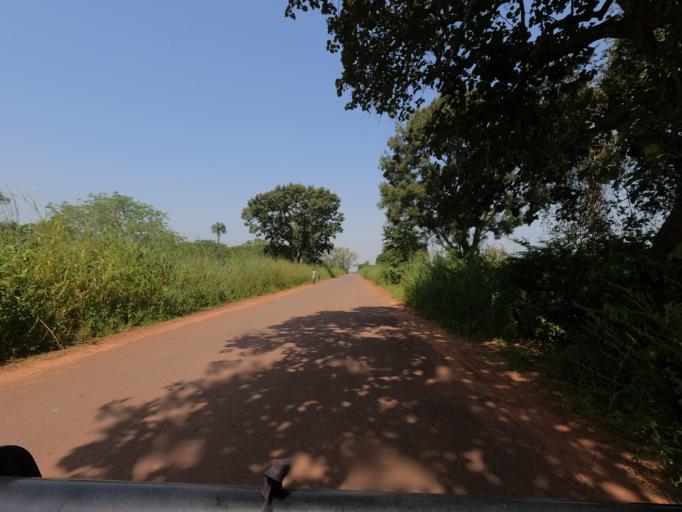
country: SN
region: Ziguinchor
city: Adeane
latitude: 12.3898
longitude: -15.7833
